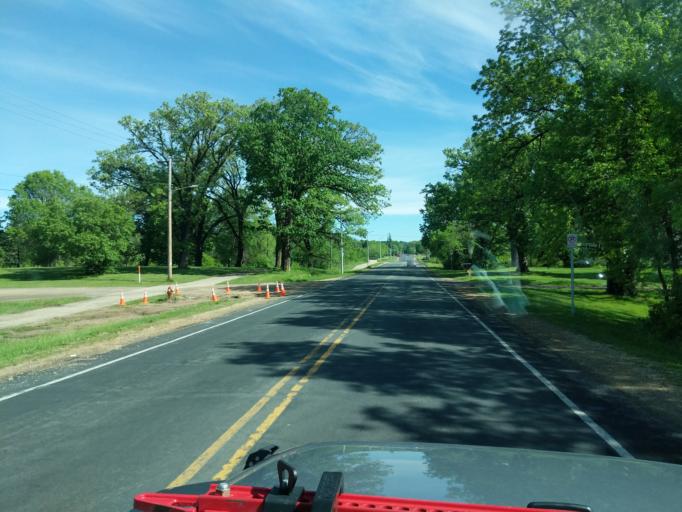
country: US
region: Wisconsin
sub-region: Pierce County
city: River Falls
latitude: 44.8466
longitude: -92.6089
